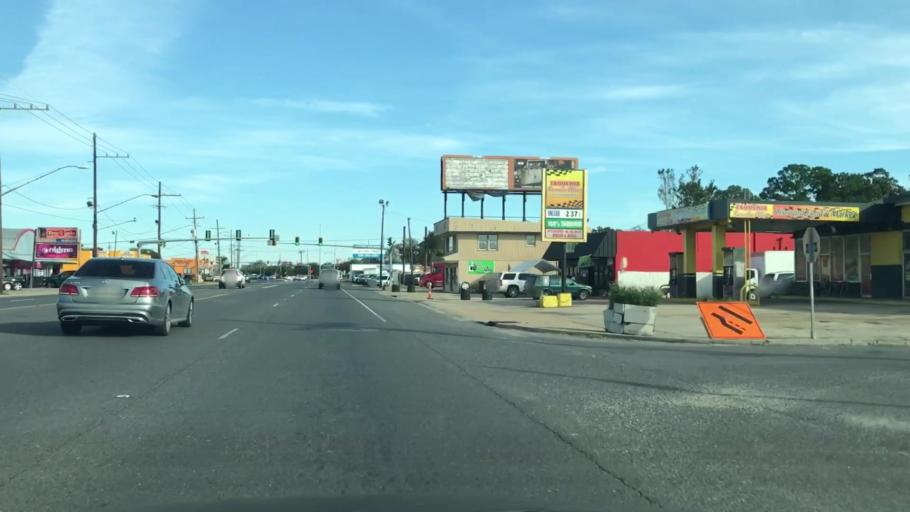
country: US
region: Louisiana
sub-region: Jefferson Parish
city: Kenner
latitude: 29.9804
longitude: -90.2483
